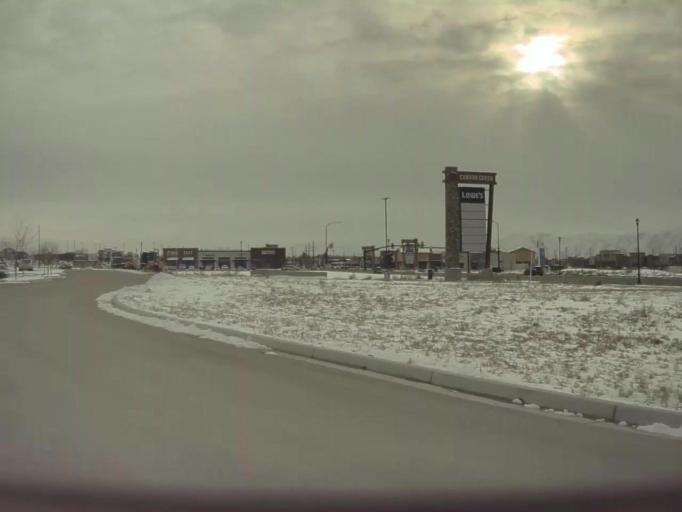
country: US
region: Utah
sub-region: Utah County
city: Spanish Fork
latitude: 40.1282
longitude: -111.6364
